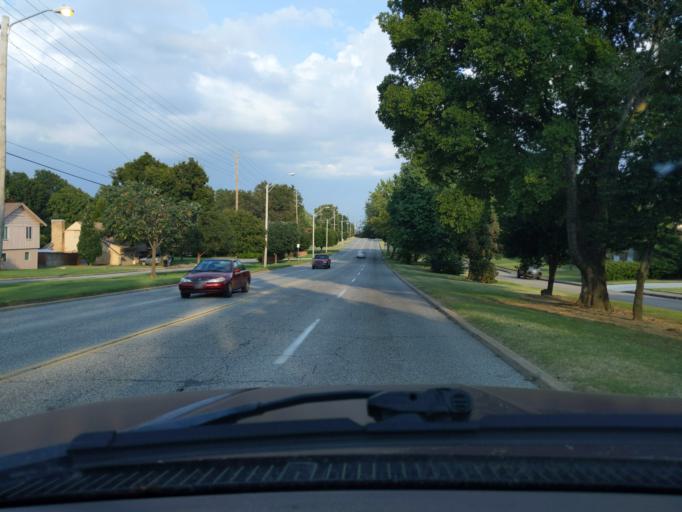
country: US
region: Oklahoma
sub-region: Tulsa County
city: Tulsa
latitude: 36.1333
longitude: -95.9154
